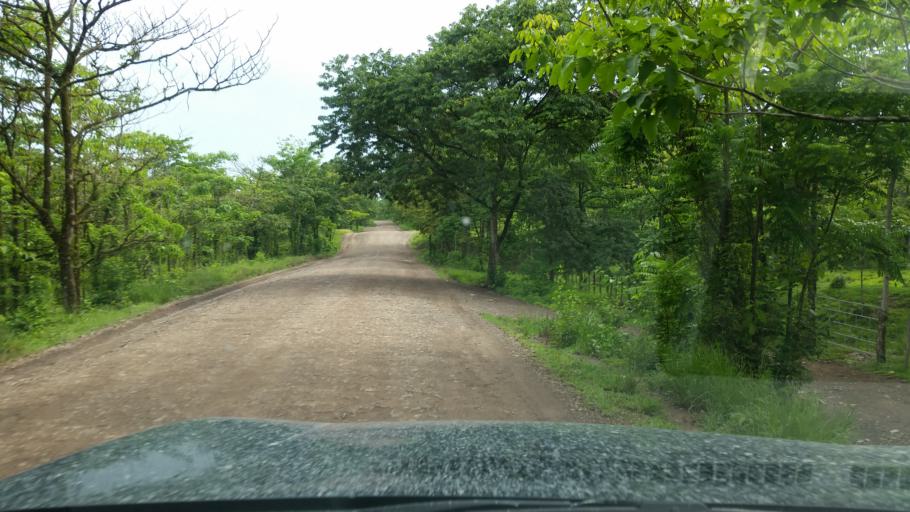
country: NI
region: Atlantico Norte (RAAN)
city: Siuna
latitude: 13.4561
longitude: -84.8507
